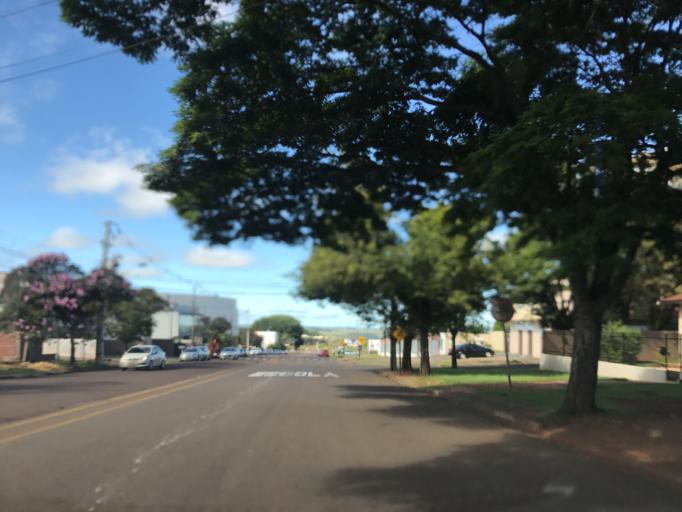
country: BR
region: Parana
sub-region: Maringa
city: Maringa
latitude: -23.4516
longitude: -51.9538
